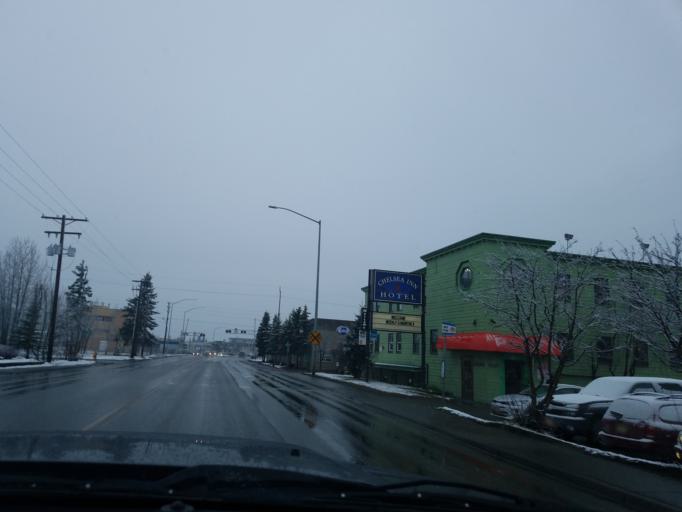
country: US
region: Alaska
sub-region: Anchorage Municipality
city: Anchorage
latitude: 61.1861
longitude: -149.9182
